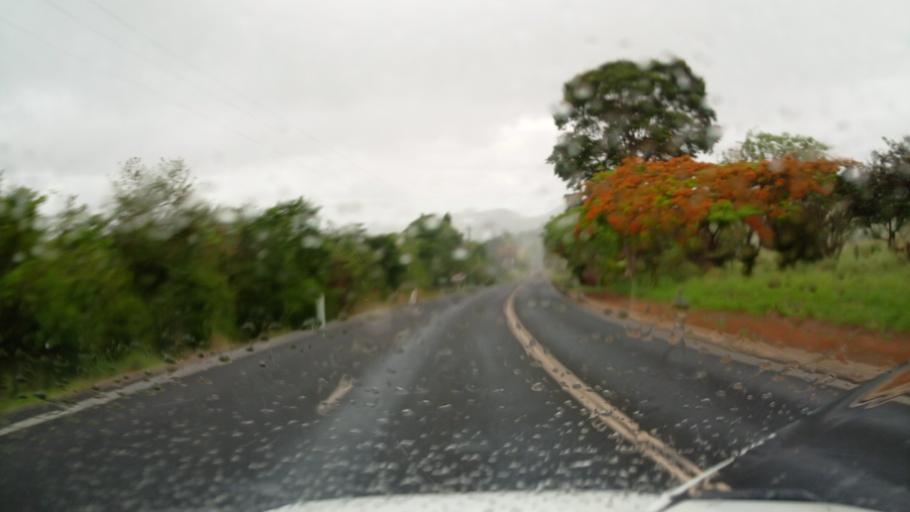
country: AU
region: Queensland
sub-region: Tablelands
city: Atherton
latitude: -17.2807
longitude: 145.5941
